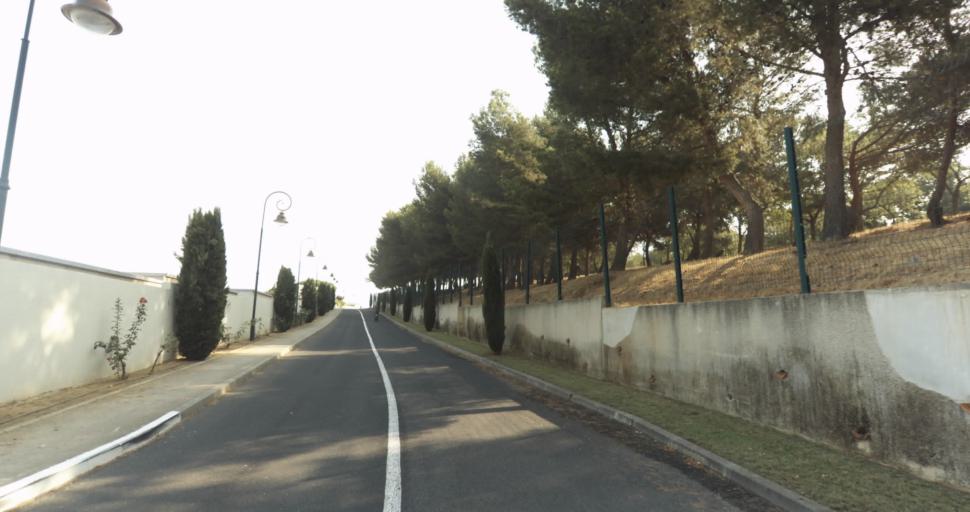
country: FR
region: Languedoc-Roussillon
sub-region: Departement des Pyrenees-Orientales
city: Latour-Bas-Elne
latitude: 42.6129
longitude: 2.9964
